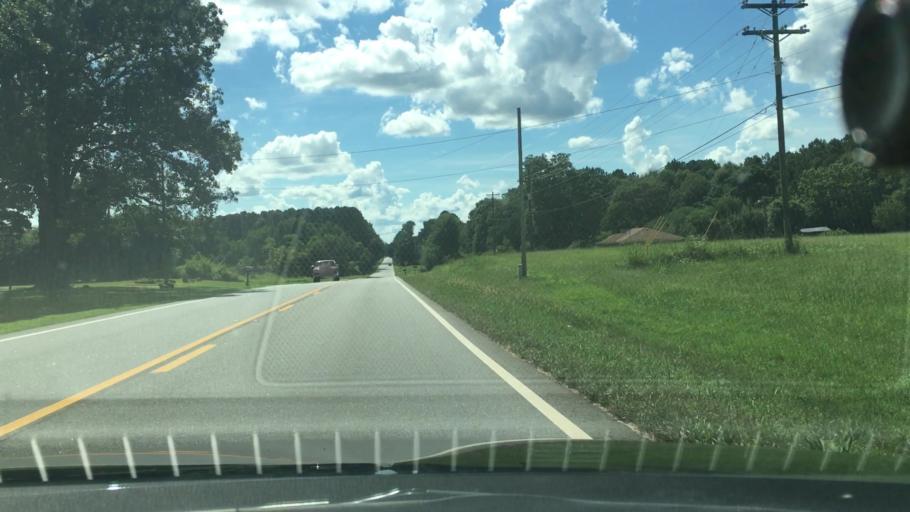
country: US
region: Georgia
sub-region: Butts County
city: Indian Springs
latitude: 33.2881
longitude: -83.8995
